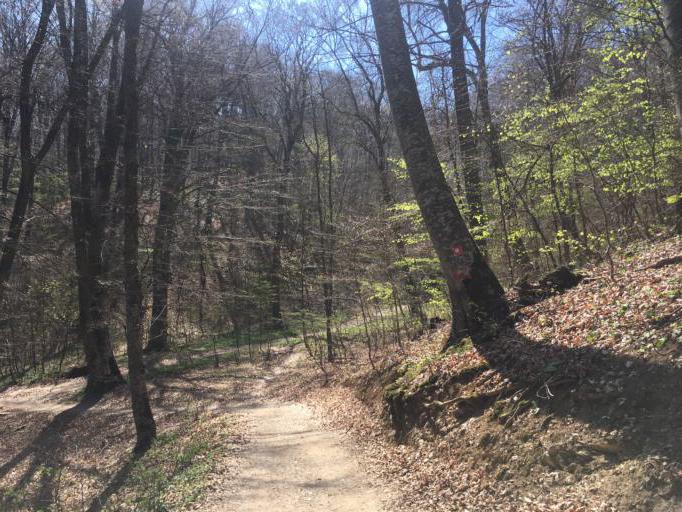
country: XK
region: Pristina
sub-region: Komuna e Prishtines
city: Pristina
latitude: 42.6632
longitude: 21.2197
